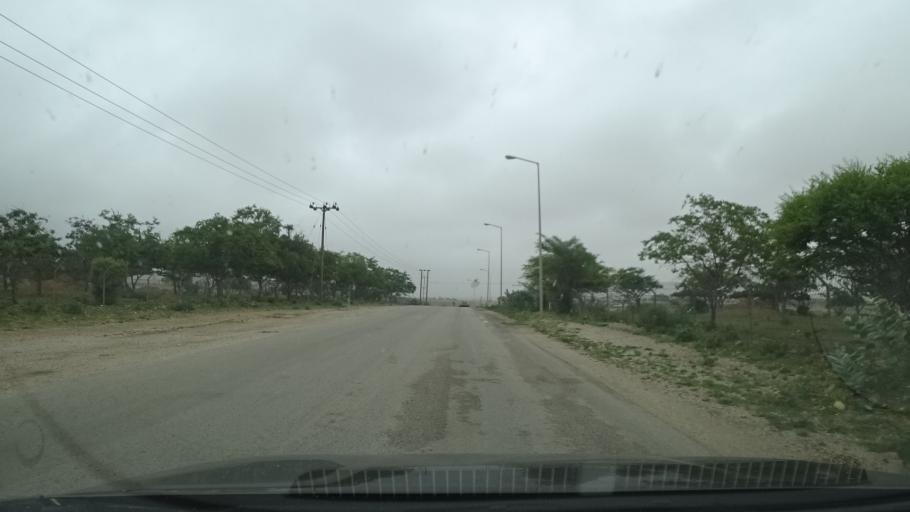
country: OM
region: Zufar
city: Salalah
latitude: 17.0874
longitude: 54.0755
